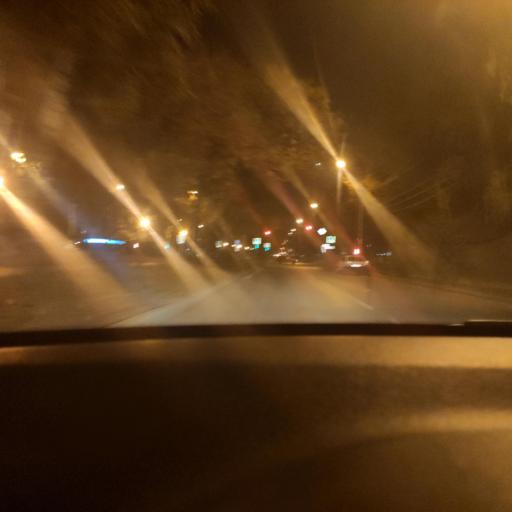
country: RU
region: Samara
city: Samara
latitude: 53.1957
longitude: 50.1789
